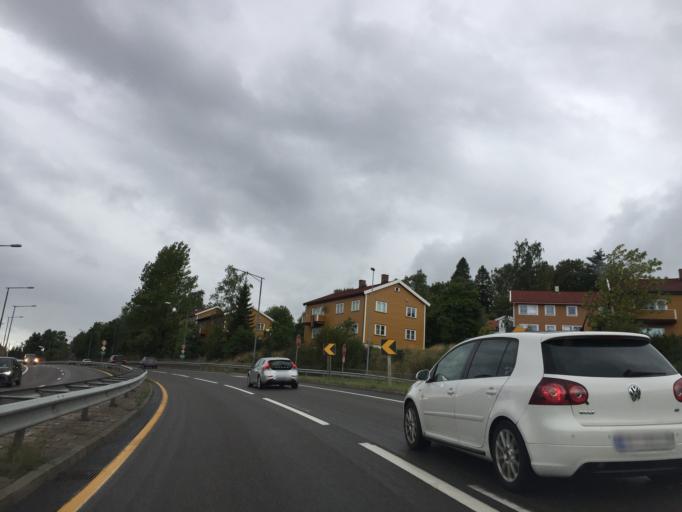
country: NO
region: Akershus
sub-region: Lorenskog
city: Kjenn
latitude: 59.9547
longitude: 10.8946
